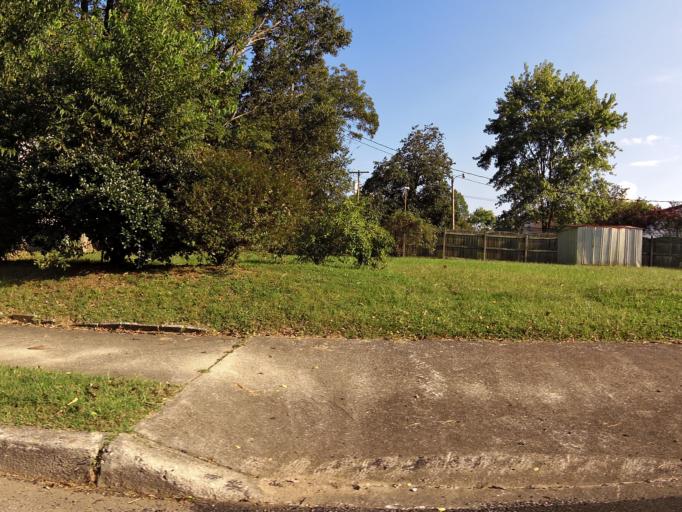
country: US
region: Tennessee
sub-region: Knox County
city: Knoxville
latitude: 36.0086
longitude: -83.9172
